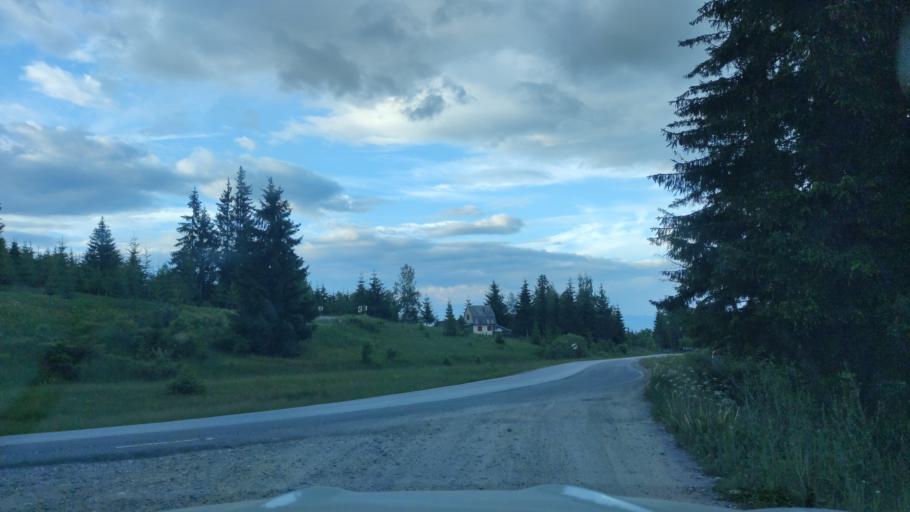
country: RO
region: Harghita
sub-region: Comuna Joseni
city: Joseni
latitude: 46.6738
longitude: 25.3679
